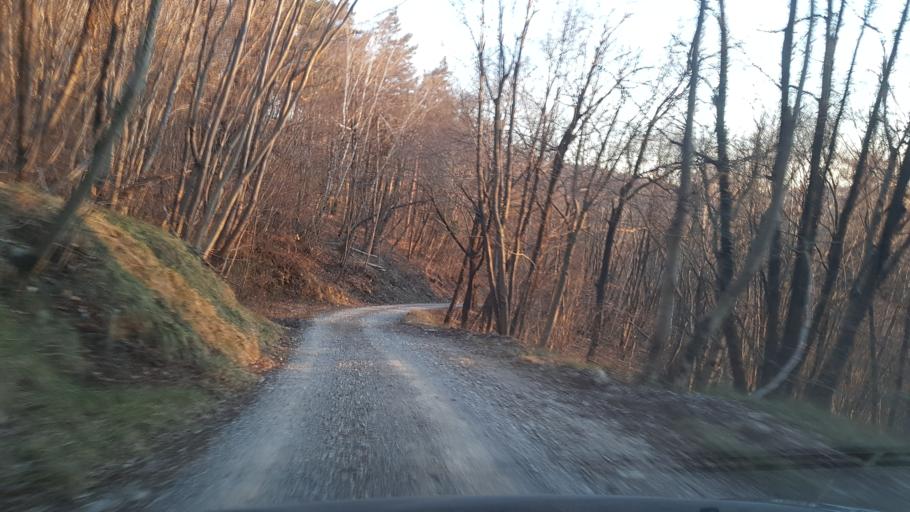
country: SI
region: Nova Gorica
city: Kromberk
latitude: 46.0123
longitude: 13.6990
